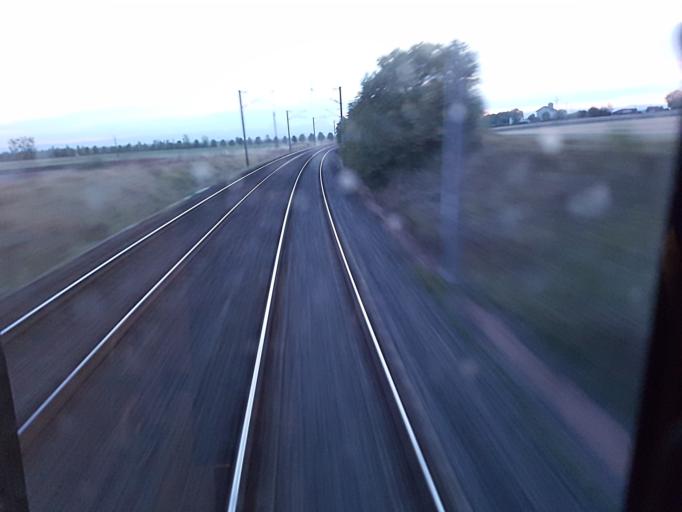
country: FR
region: Auvergne
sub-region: Departement du Puy-de-Dome
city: Randan
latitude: 45.9868
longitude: 3.3184
